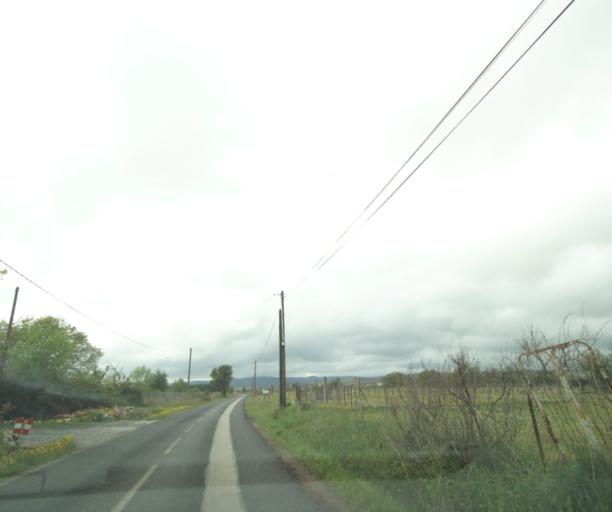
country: FR
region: Languedoc-Roussillon
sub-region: Departement de l'Herault
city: Cournonterral
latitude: 43.5564
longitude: 3.7444
